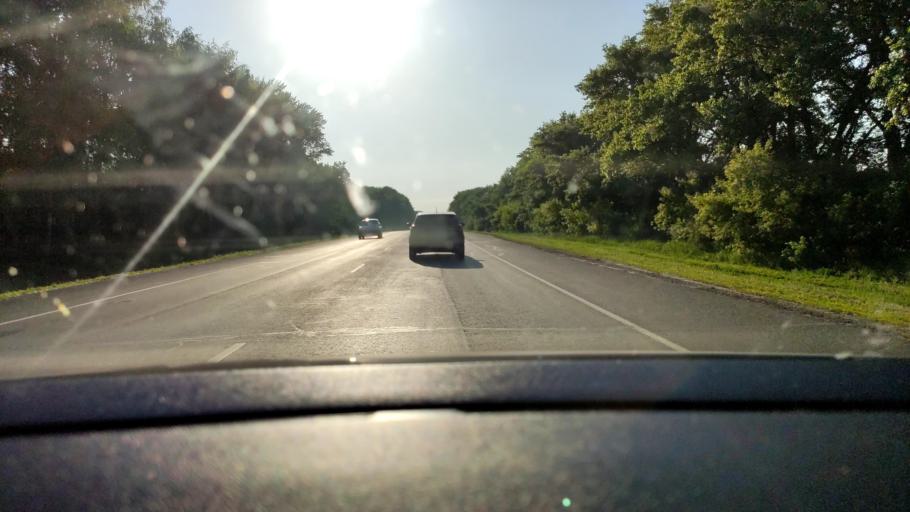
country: RU
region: Voronezj
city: Kashirskoye
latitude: 51.4936
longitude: 39.6055
